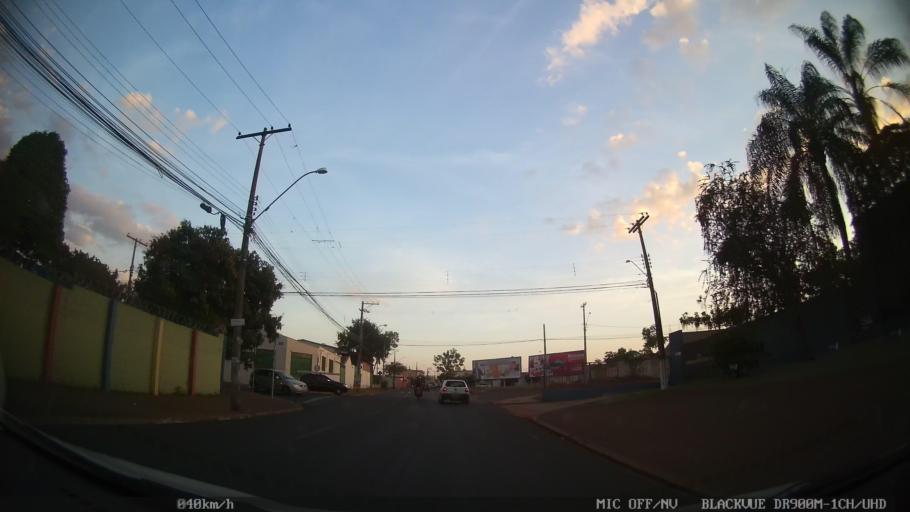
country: BR
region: Sao Paulo
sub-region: Ribeirao Preto
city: Ribeirao Preto
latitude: -21.1364
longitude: -47.8187
